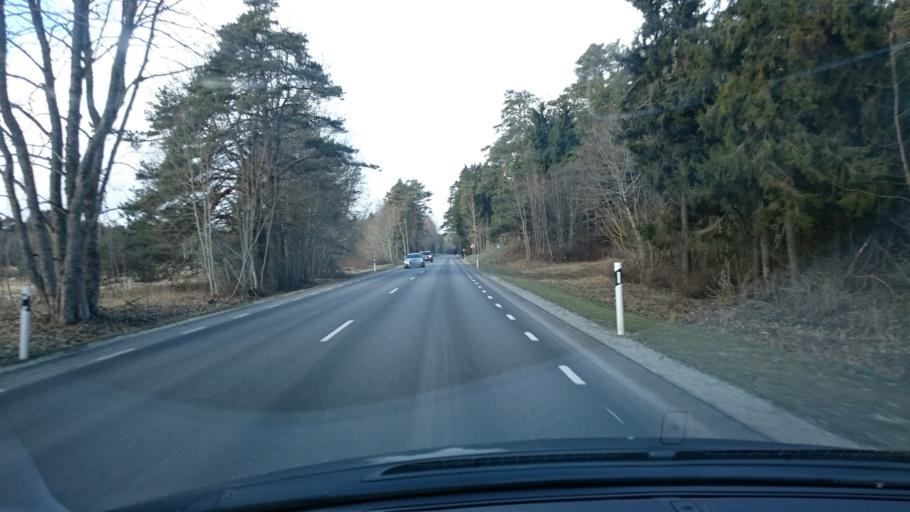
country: EE
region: Harju
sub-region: Keila linn
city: Keila
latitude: 59.3952
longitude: 24.2791
